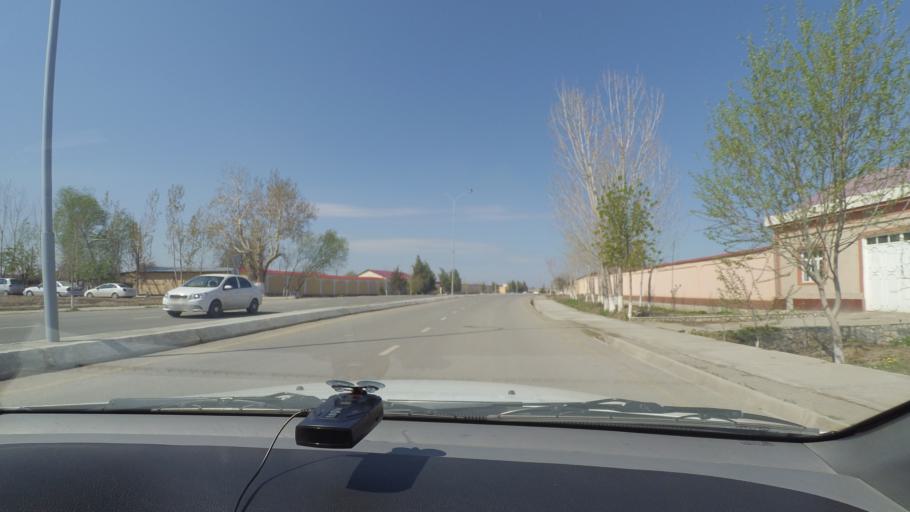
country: UZ
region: Bukhara
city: Kogon
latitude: 39.8006
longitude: 64.5269
